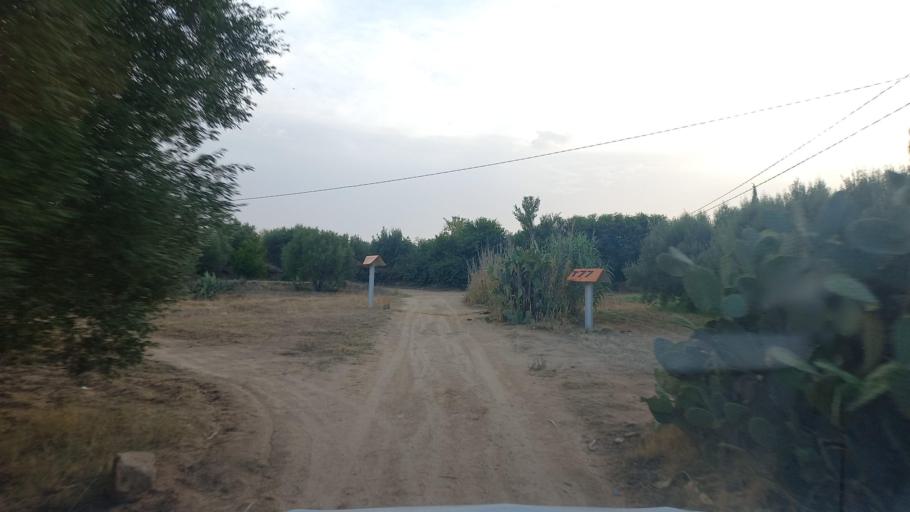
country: TN
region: Al Qasrayn
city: Kasserine
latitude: 35.2142
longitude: 9.0512
